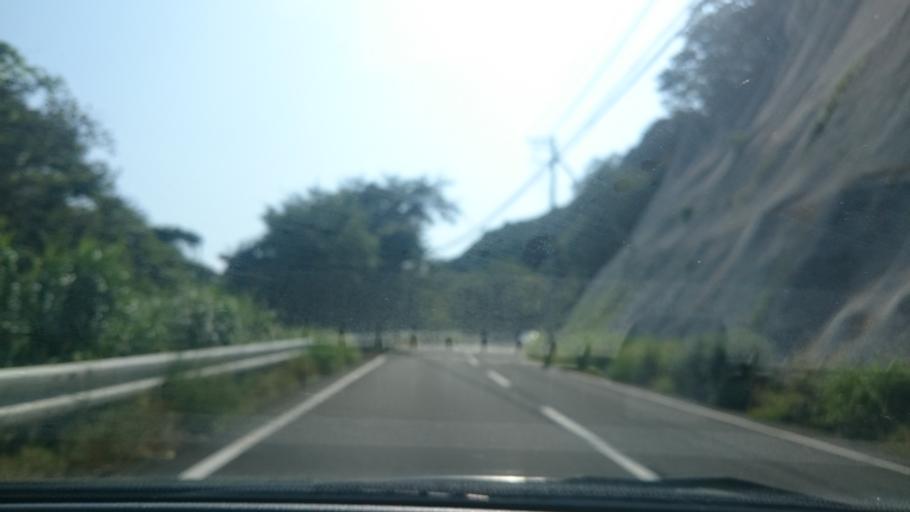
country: JP
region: Shizuoka
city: Heda
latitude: 34.9515
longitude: 138.7745
